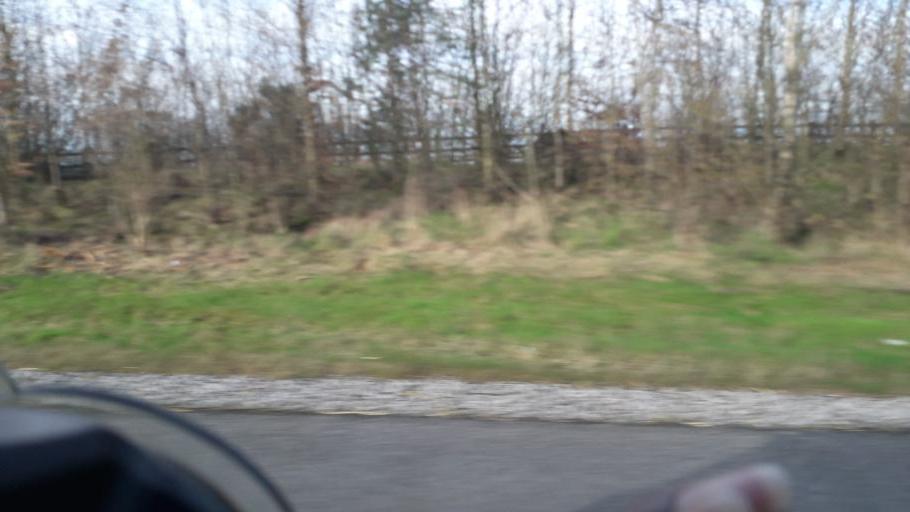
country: IE
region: Leinster
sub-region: Lu
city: Dundalk
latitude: 54.0135
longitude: -6.4454
